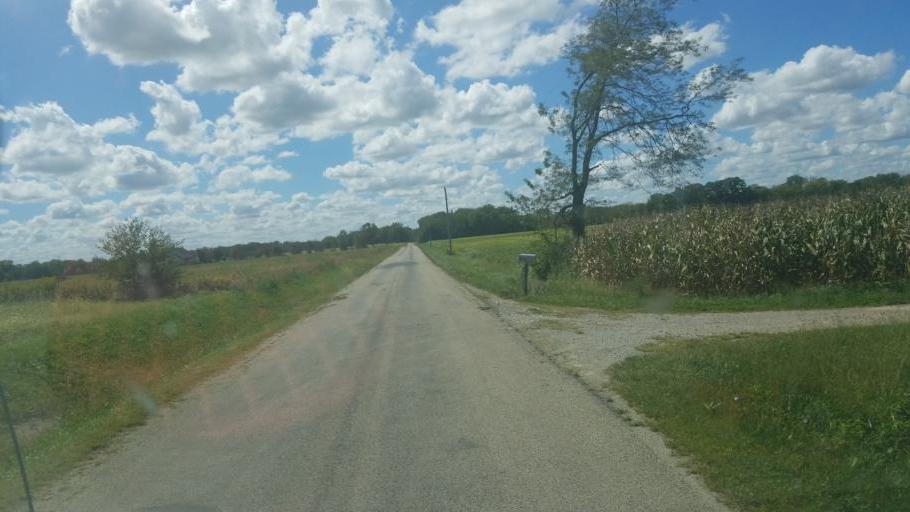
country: US
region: Ohio
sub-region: Madison County
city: Choctaw Lake
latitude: 40.0164
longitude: -83.3735
